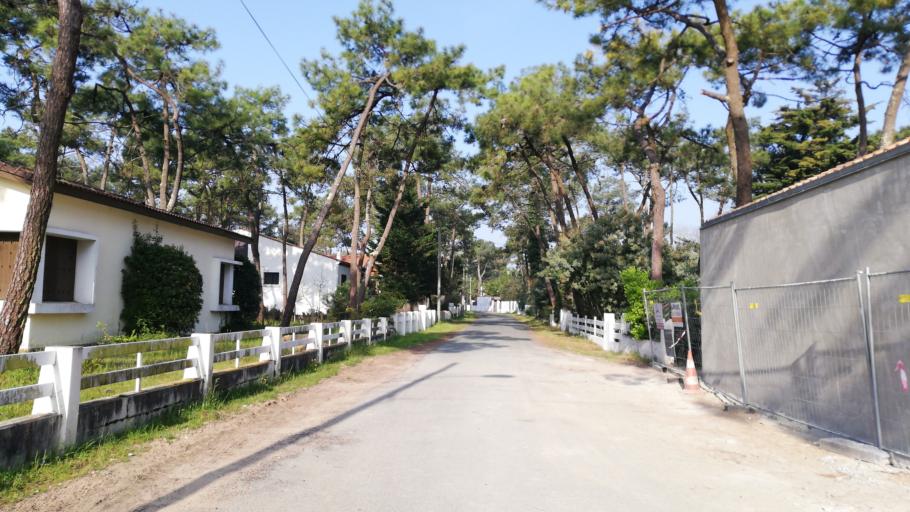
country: FR
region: Pays de la Loire
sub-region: Departement de la Vendee
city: La Tranche-sur-Mer
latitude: 46.3473
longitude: -1.4124
